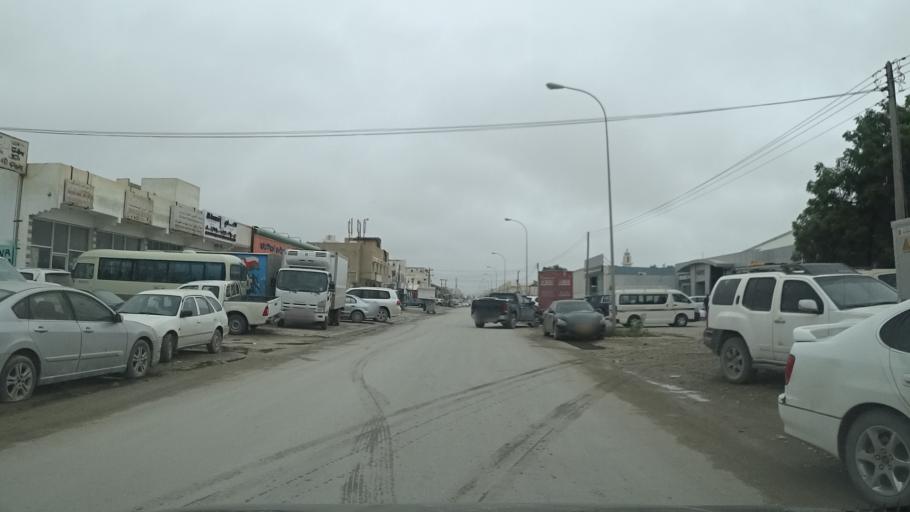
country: OM
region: Zufar
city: Salalah
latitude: 17.0181
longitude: 54.0467
